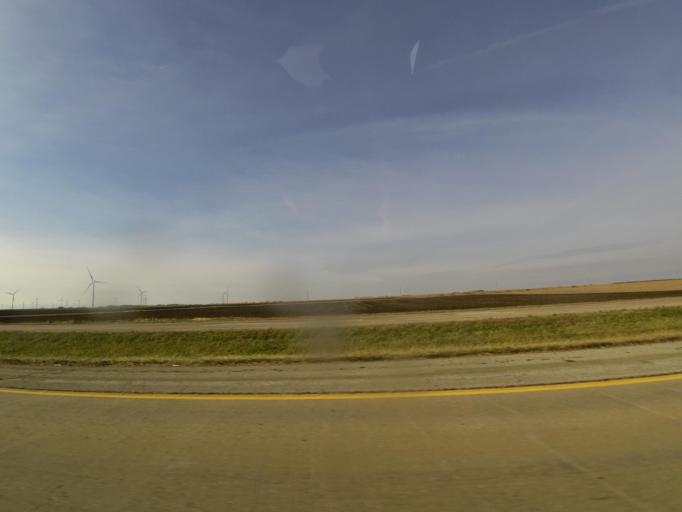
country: US
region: Illinois
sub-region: Macon County
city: Maroa
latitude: 40.0580
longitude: -88.9656
